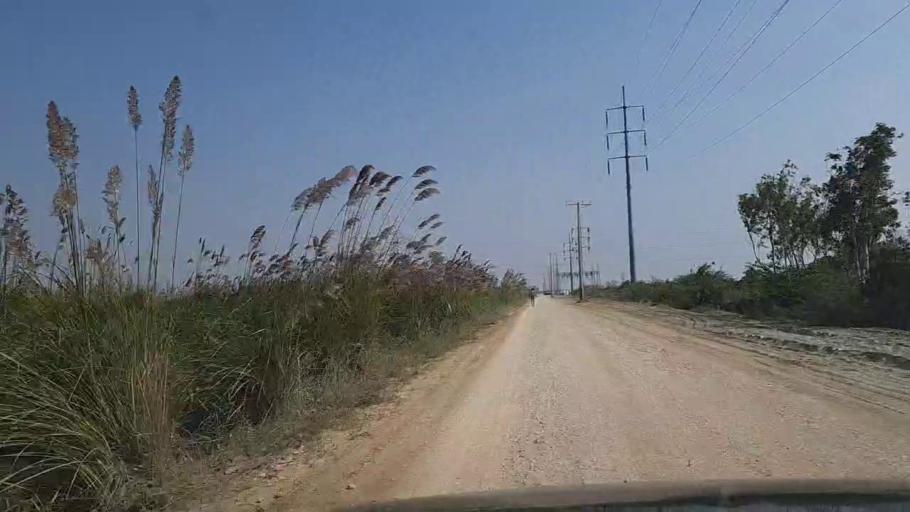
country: PK
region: Sindh
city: Gharo
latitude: 24.7219
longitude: 67.5426
